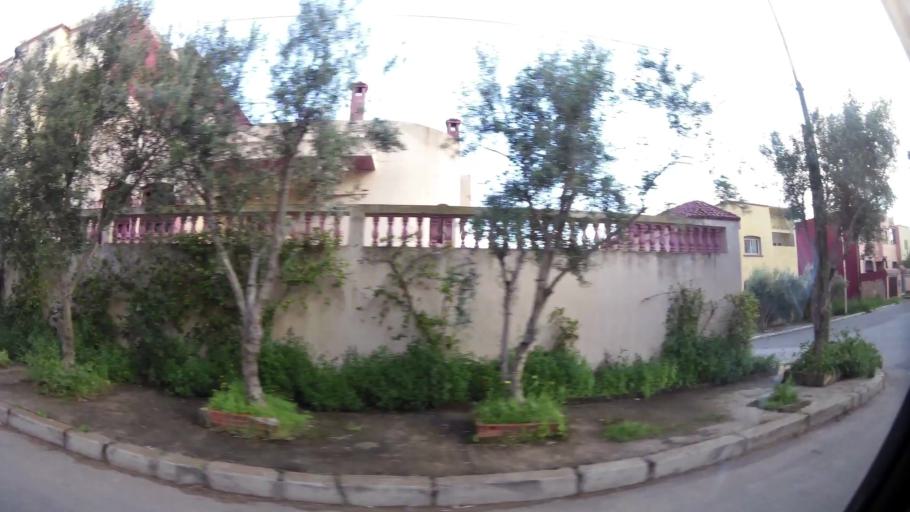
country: MA
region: Chaouia-Ouardigha
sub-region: Settat Province
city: Settat
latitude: 33.0083
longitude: -7.6371
